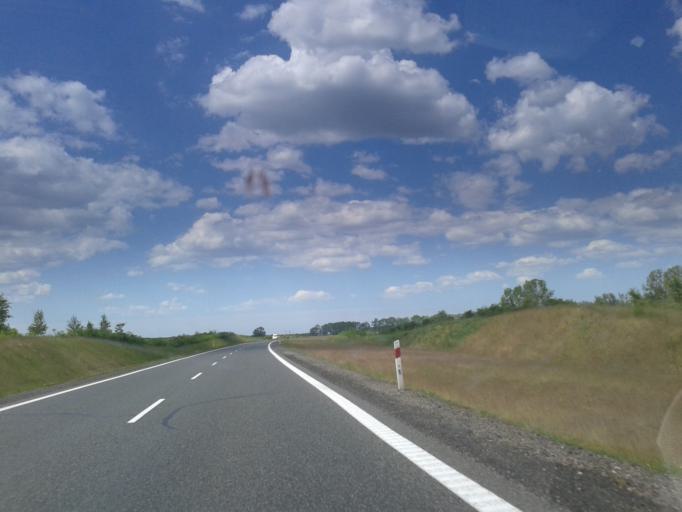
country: PL
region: Pomeranian Voivodeship
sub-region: Powiat chojnicki
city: Chojnice
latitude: 53.6854
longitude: 17.4898
